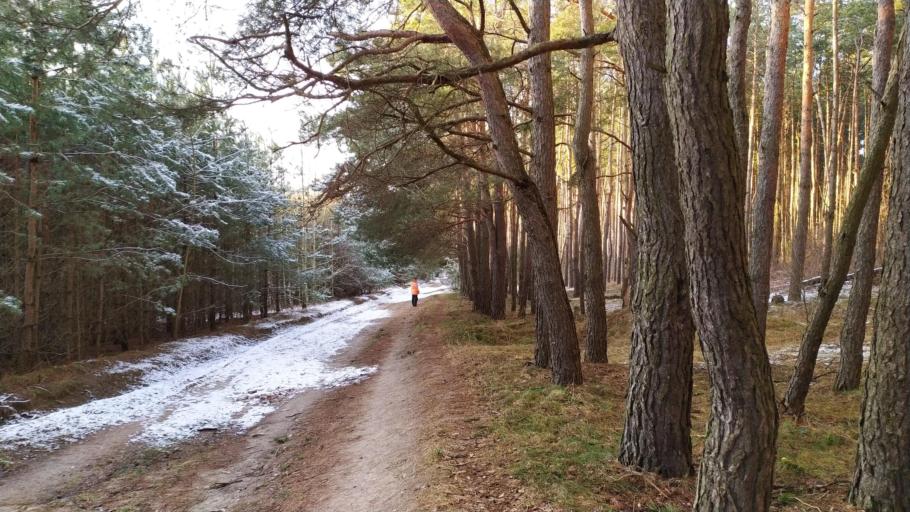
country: BY
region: Brest
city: Kamyanyets
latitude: 52.3835
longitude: 23.8319
